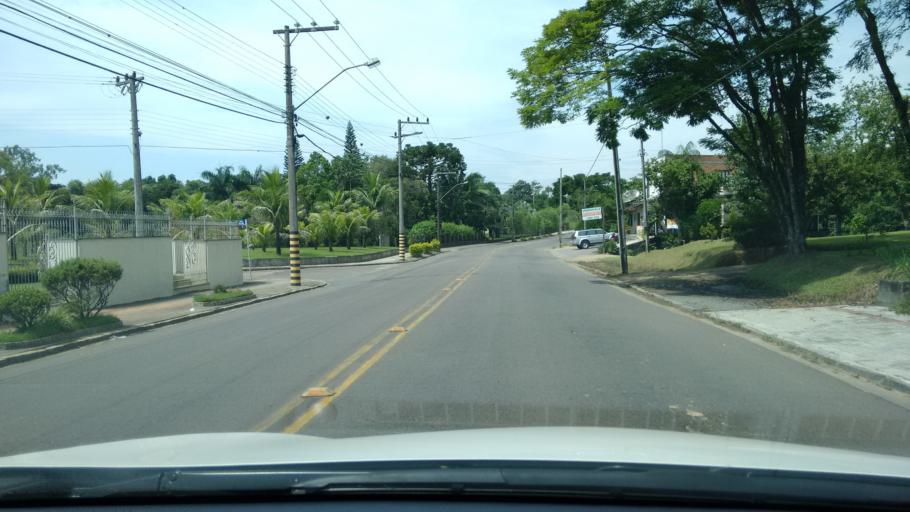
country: BR
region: Santa Catarina
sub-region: Timbo
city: Timbo
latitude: -26.8283
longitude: -49.2836
